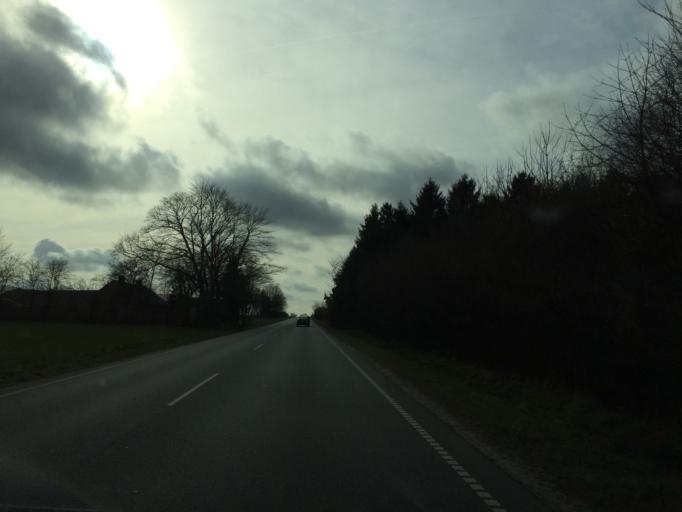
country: DK
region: Central Jutland
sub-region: Norddjurs Kommune
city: Allingabro
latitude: 56.4451
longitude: 10.2490
